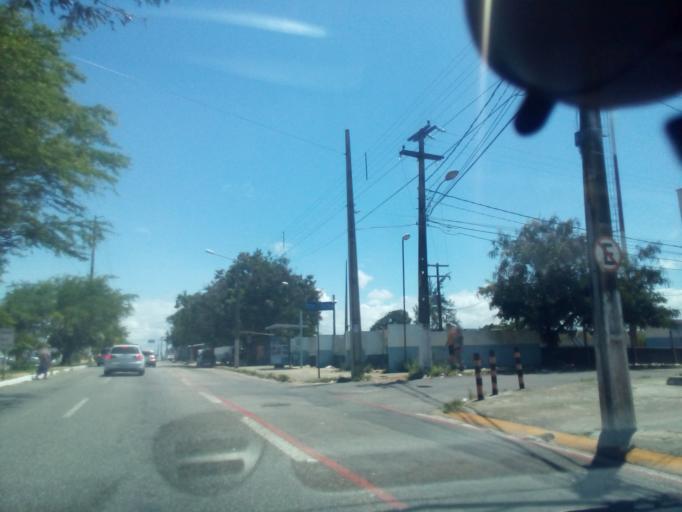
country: BR
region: Rio Grande do Norte
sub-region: Natal
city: Natal
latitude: -5.8390
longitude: -35.2203
